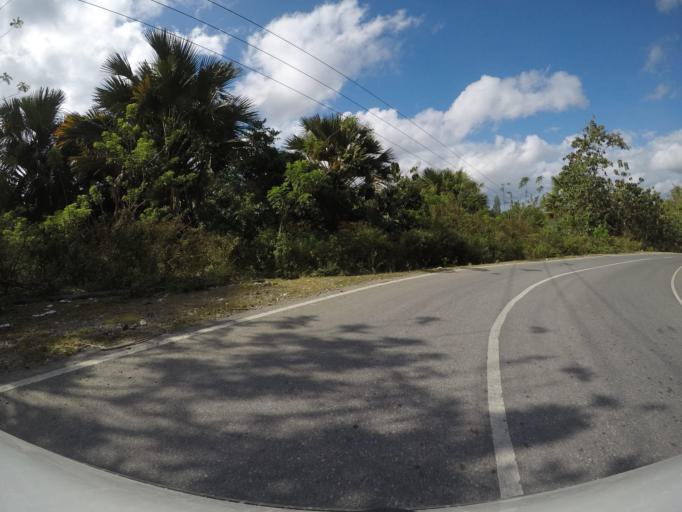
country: TL
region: Viqueque
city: Viqueque
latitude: -8.8759
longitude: 126.3768
